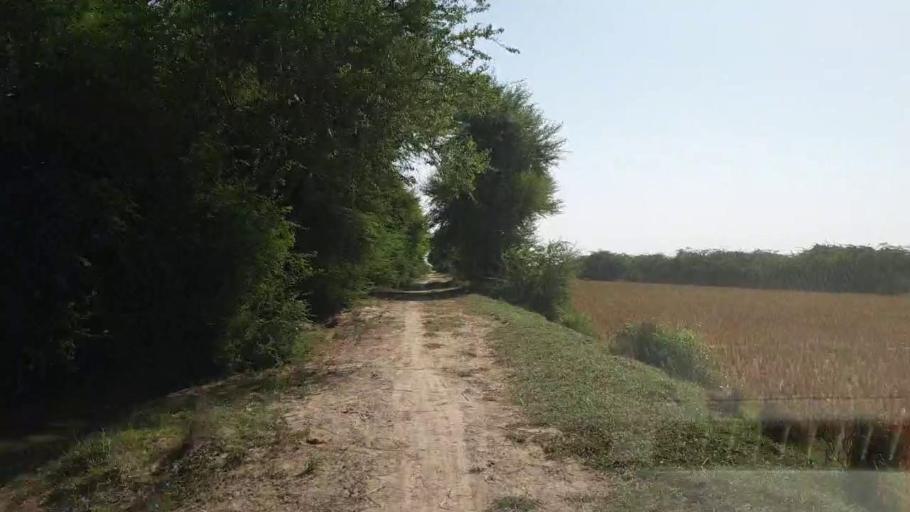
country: PK
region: Sindh
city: Kadhan
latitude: 24.6272
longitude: 68.9941
